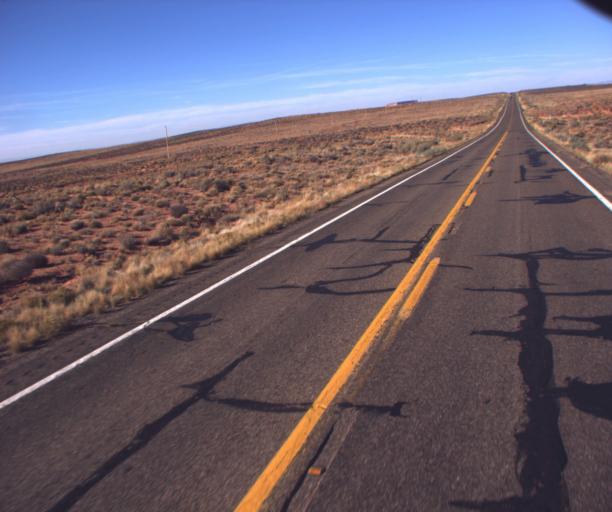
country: US
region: Arizona
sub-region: Coconino County
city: LeChee
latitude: 36.7607
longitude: -111.2851
